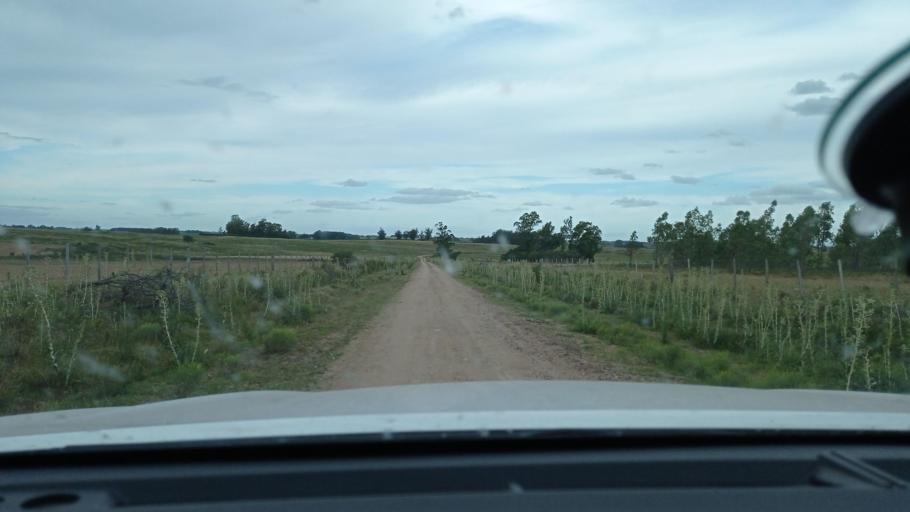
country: UY
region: Florida
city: Casupa
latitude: -34.1242
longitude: -55.8096
